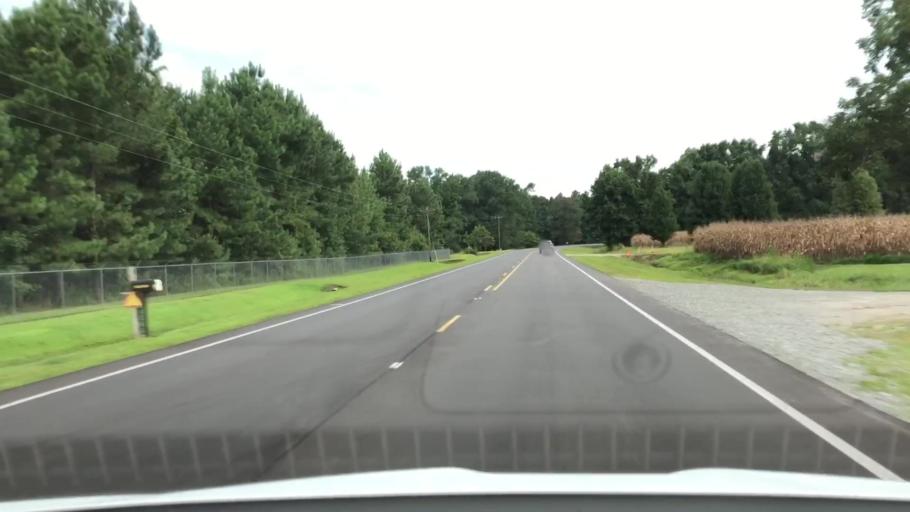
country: US
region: North Carolina
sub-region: Jones County
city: Maysville
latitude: 34.8856
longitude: -77.2116
